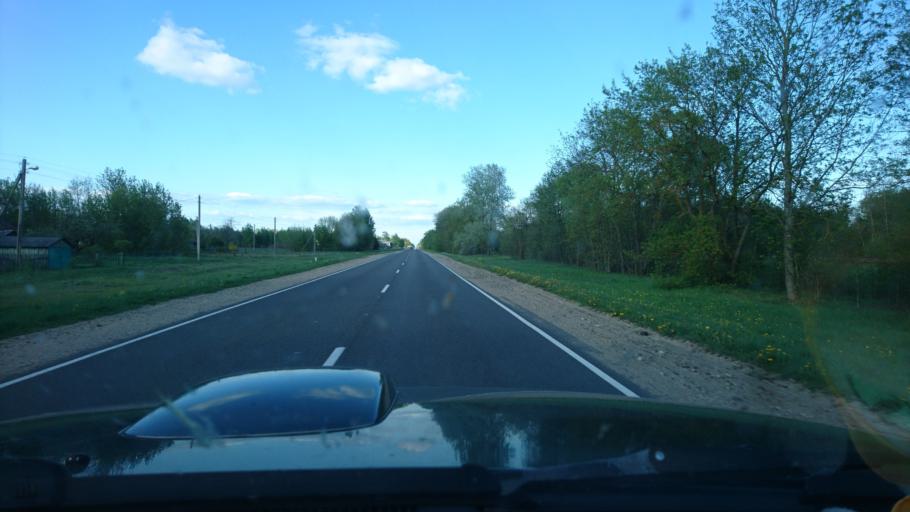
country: BY
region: Brest
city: Nyakhachava
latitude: 52.6426
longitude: 25.2026
